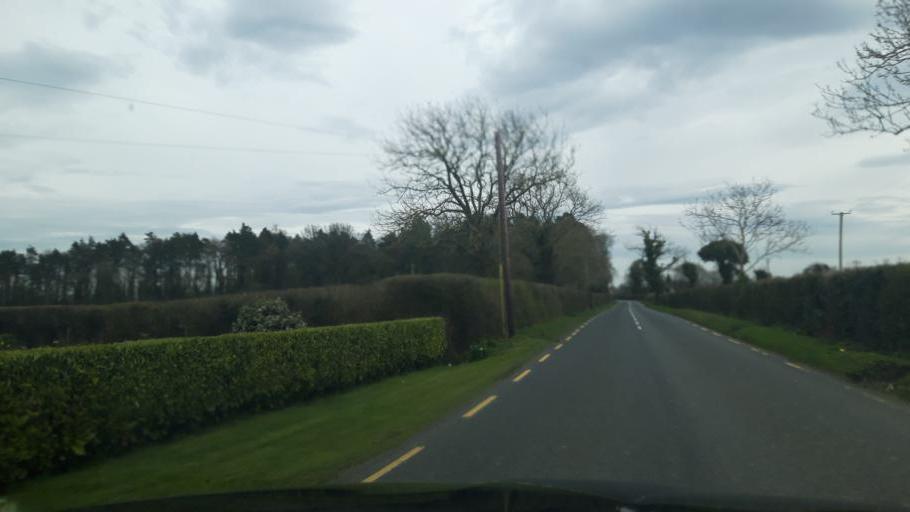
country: IE
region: Leinster
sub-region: Kildare
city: Maynooth
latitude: 53.3550
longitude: -6.6250
